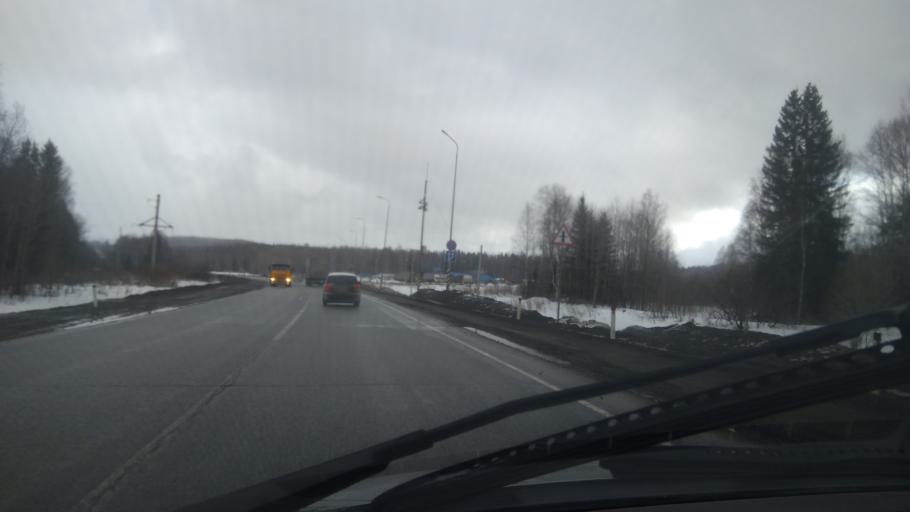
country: RU
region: Sverdlovsk
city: Ufimskiy
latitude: 56.7828
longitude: 58.3979
